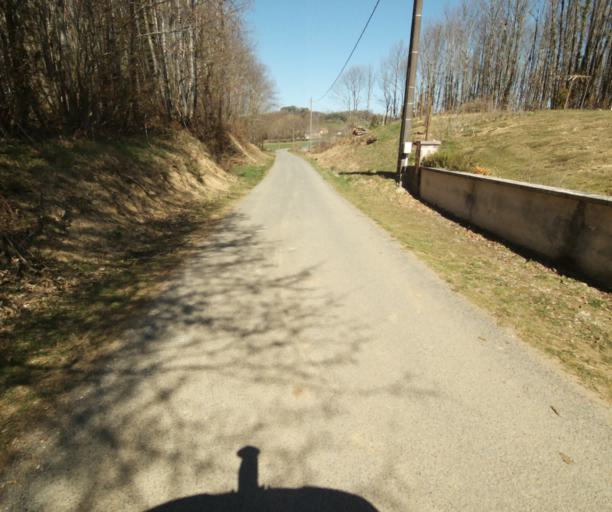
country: FR
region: Limousin
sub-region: Departement de la Correze
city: Saint-Clement
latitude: 45.3358
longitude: 1.6941
